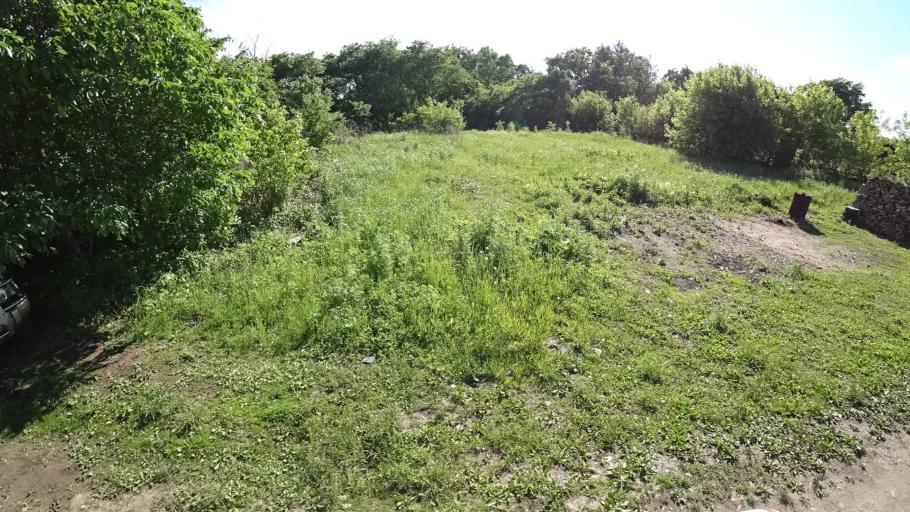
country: RU
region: Khabarovsk Krai
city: Khor
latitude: 47.8871
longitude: 134.9903
